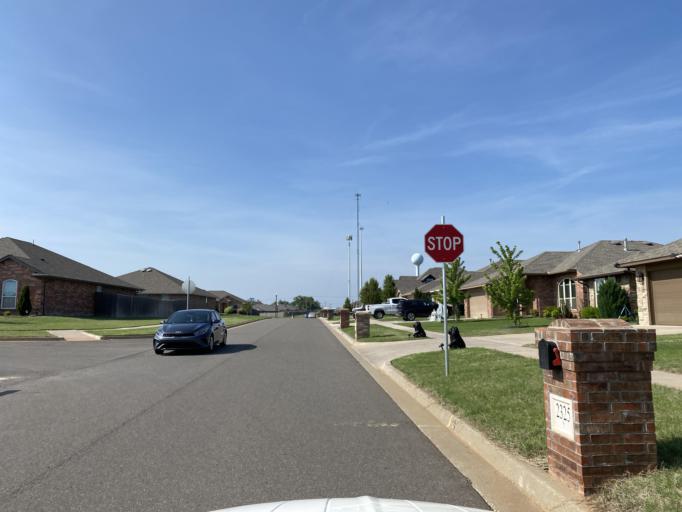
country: US
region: Oklahoma
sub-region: Oklahoma County
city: Nicoma Park
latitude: 35.4398
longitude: -97.3410
